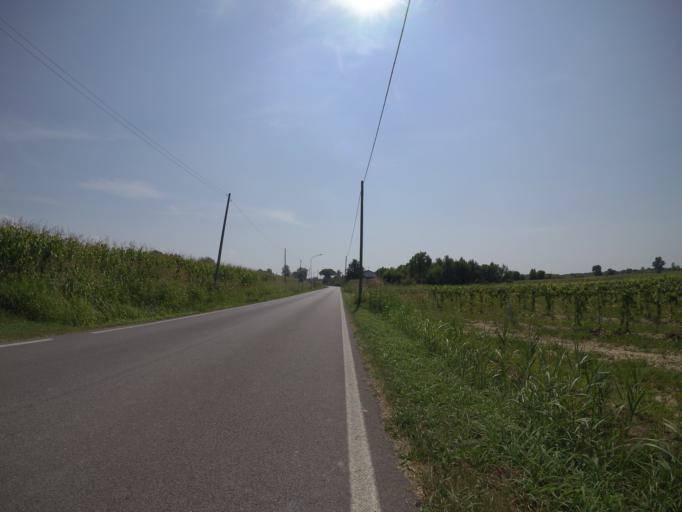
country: IT
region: Friuli Venezia Giulia
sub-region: Provincia di Udine
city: Pocenia
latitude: 45.8449
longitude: 13.0950
